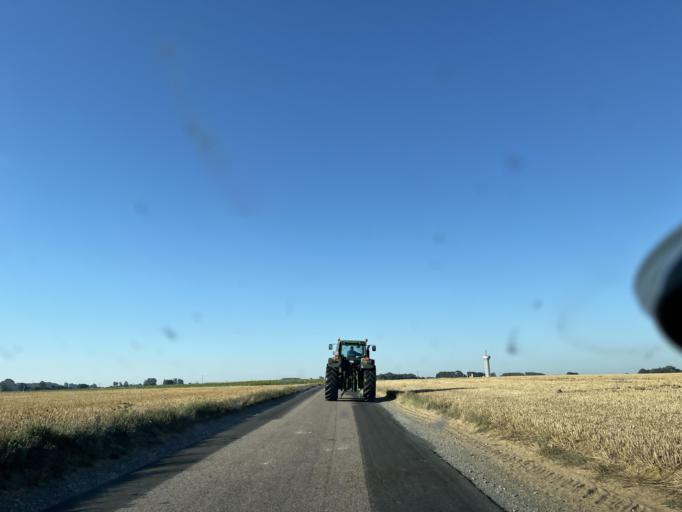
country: FR
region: Haute-Normandie
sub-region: Departement de la Seine-Maritime
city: Fauville-en-Caux
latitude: 49.6186
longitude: 0.6122
